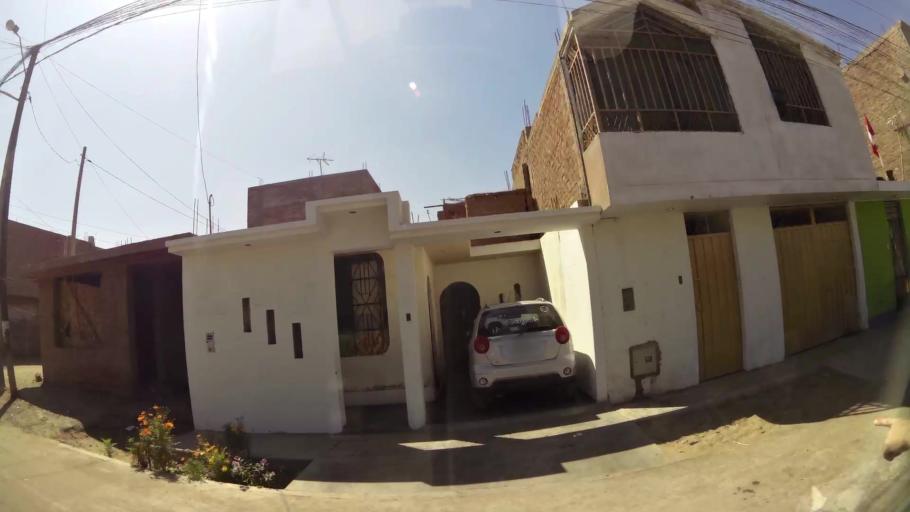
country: PE
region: Ica
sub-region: Provincia de Ica
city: Subtanjalla
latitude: -14.0392
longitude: -75.7485
